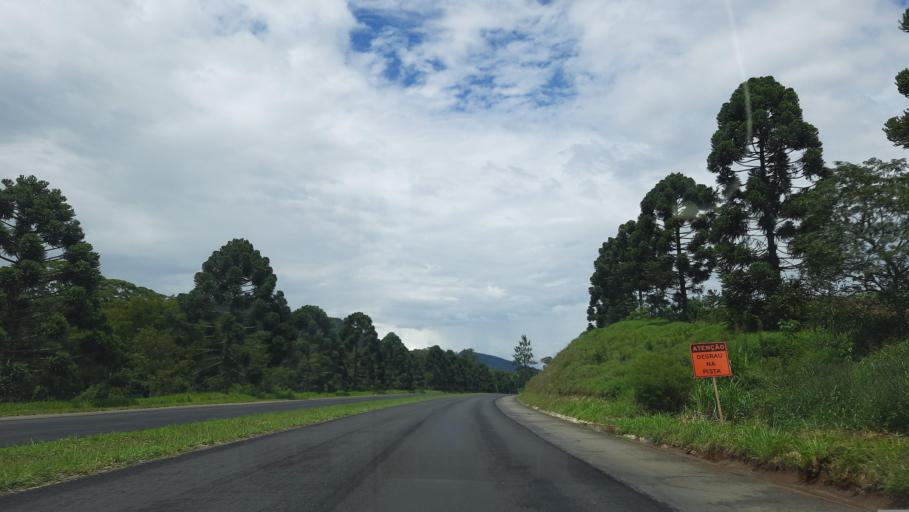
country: BR
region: Minas Gerais
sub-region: Pocos De Caldas
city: Pocos de Caldas
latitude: -21.8127
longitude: -46.6588
